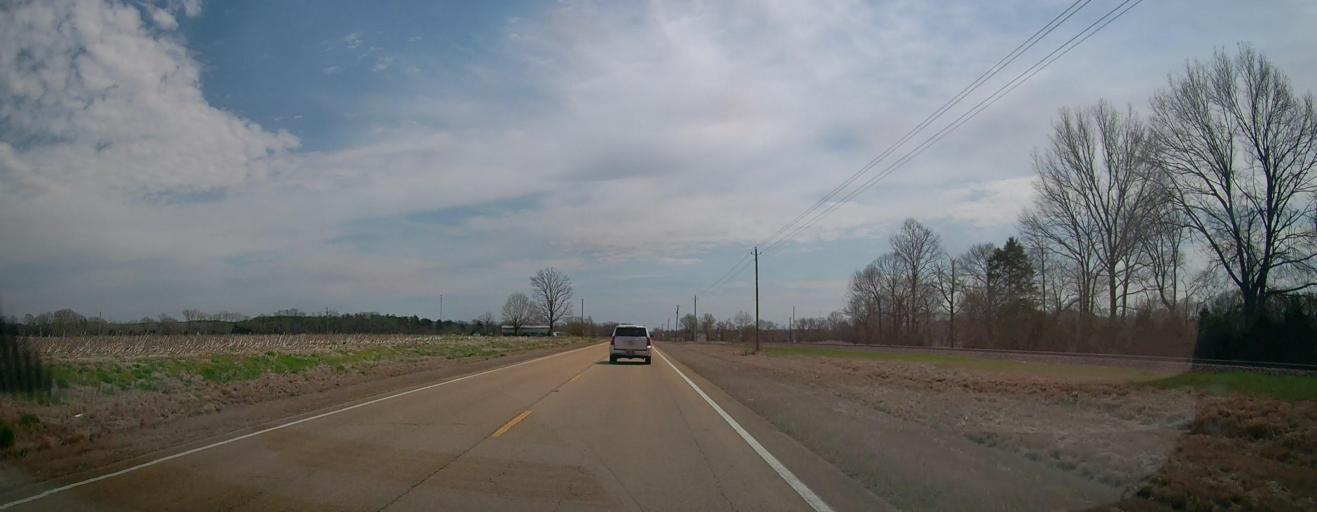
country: US
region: Mississippi
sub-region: Benton County
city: Ashland
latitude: 34.6234
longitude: -89.2435
